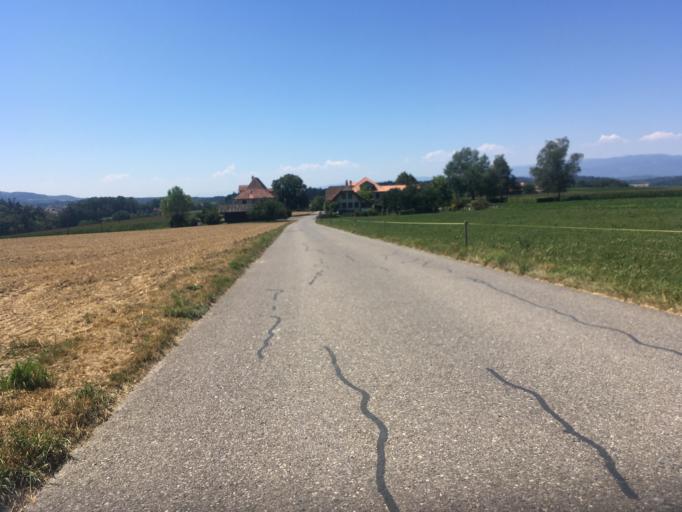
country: CH
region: Solothurn
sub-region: Bezirk Bucheggberg
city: Messen
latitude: 47.0755
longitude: 7.4256
